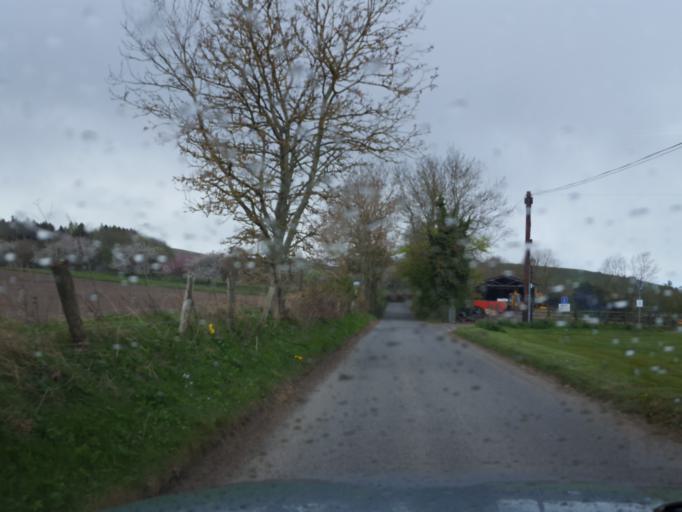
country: GB
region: Scotland
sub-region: Perth and Kinross
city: Errol
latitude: 56.4263
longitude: -3.2545
